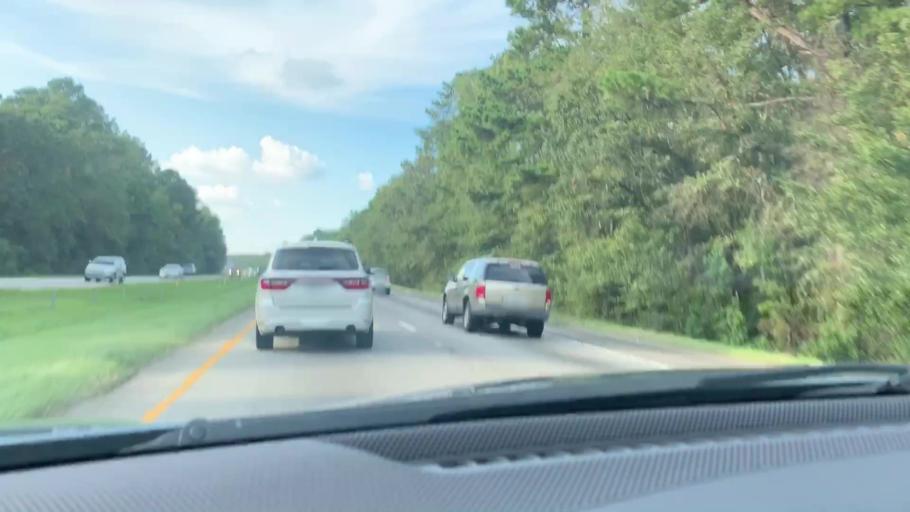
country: US
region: South Carolina
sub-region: Orangeburg County
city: Brookdale
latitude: 33.4943
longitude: -80.7653
